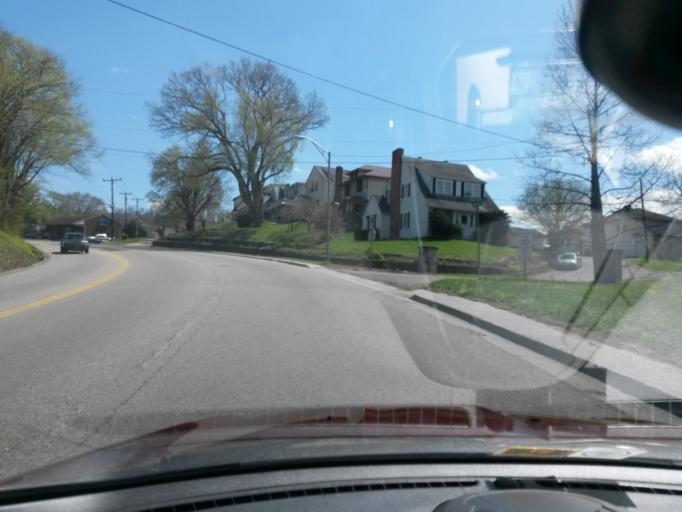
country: US
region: Virginia
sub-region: City of Covington
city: Fairlawn
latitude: 37.7786
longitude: -79.9868
